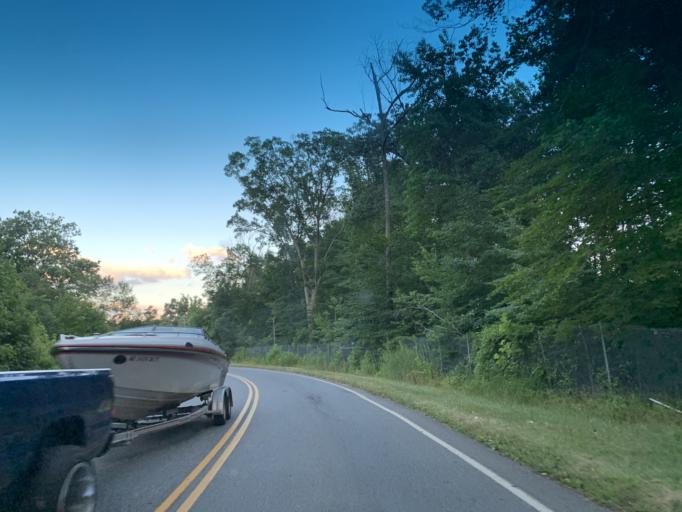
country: US
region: Maryland
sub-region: Harford County
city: Aberdeen
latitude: 39.5285
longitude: -76.1449
